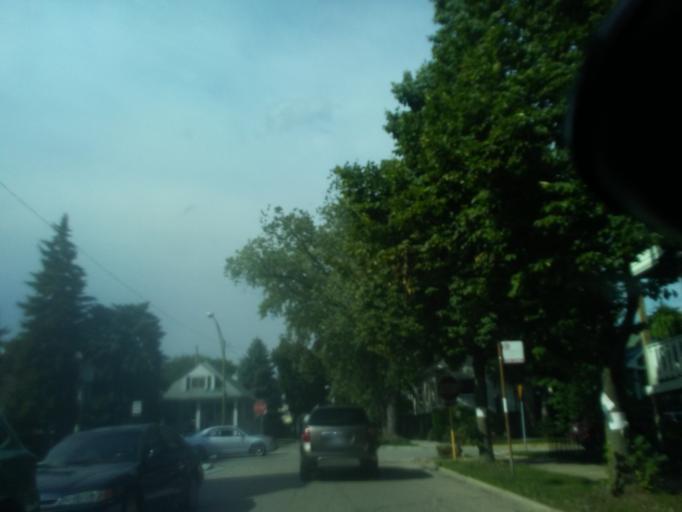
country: US
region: Illinois
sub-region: Cook County
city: Lincolnwood
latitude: 41.9686
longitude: -87.7527
